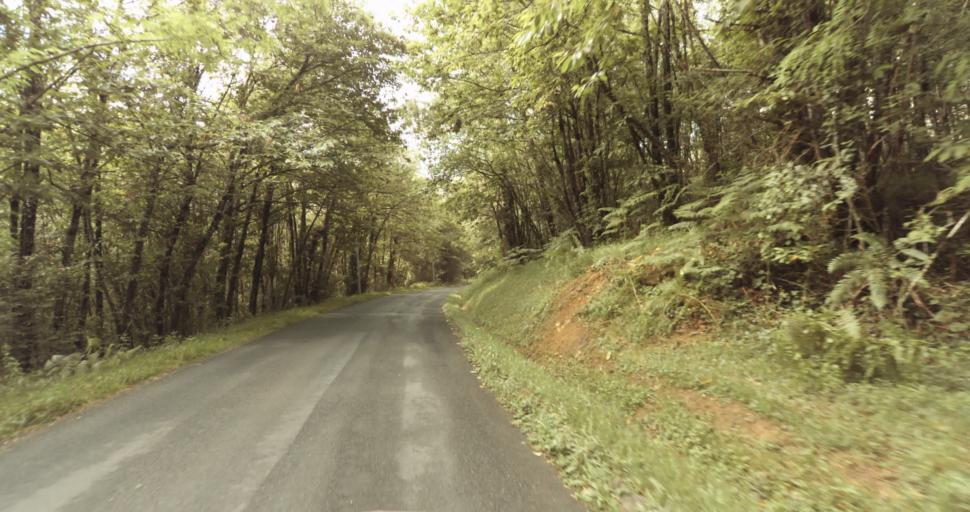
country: FR
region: Aquitaine
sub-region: Departement de la Dordogne
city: Le Bugue
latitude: 44.9327
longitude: 0.8184
